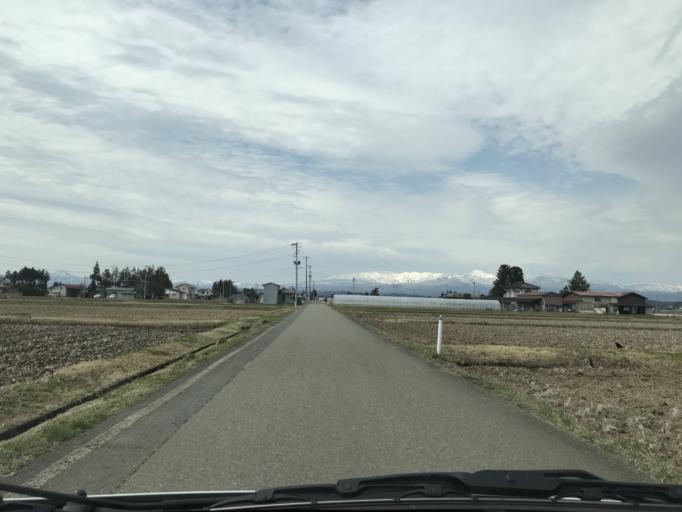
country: JP
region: Iwate
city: Mizusawa
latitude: 39.1496
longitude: 141.1076
